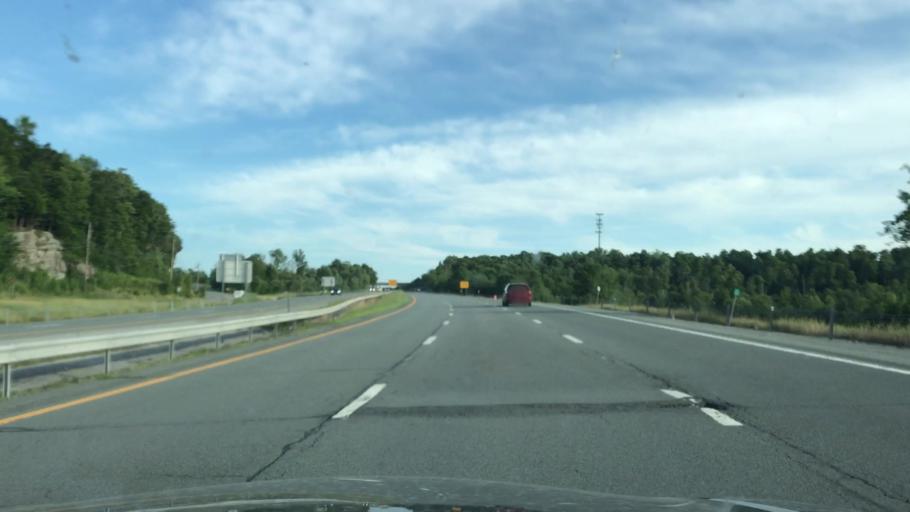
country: US
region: New York
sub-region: Sullivan County
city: Monticello
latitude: 41.7029
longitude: -74.7361
